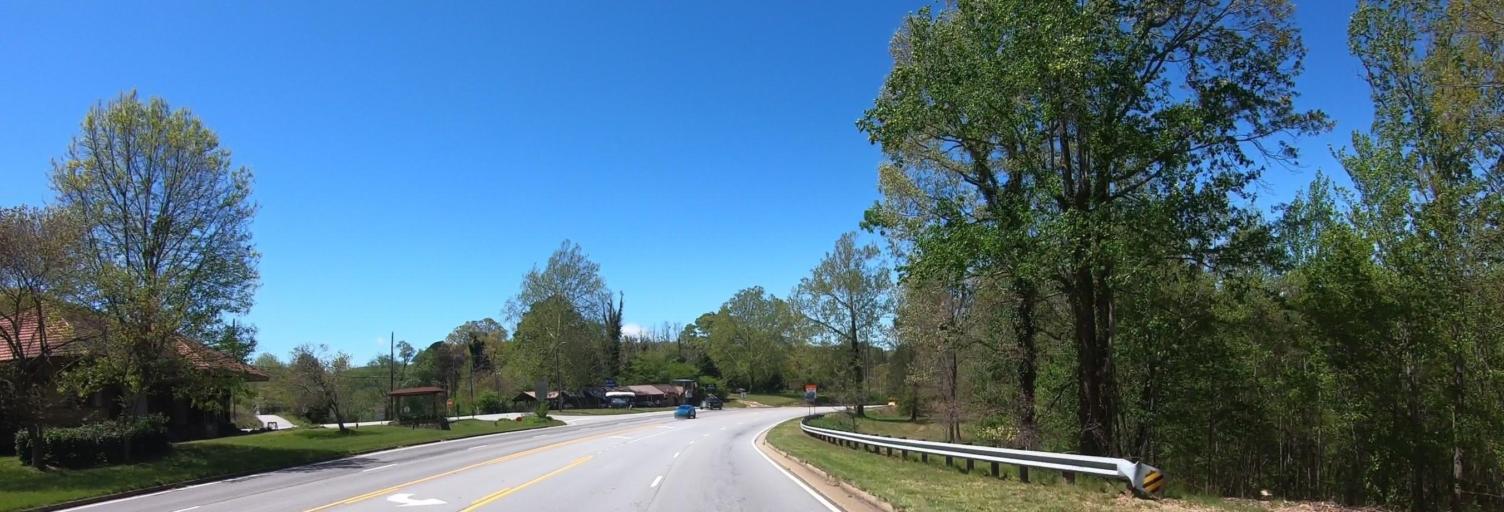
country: US
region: Georgia
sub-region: Rabun County
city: Clayton
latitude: 34.7365
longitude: -83.3918
